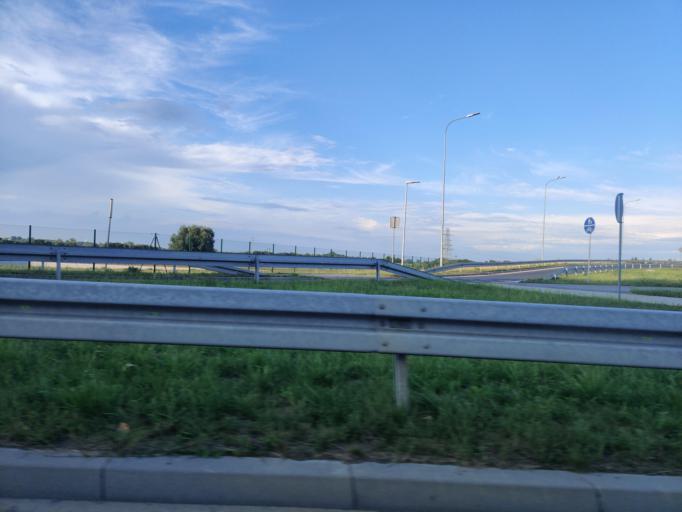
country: PL
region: Greater Poland Voivodeship
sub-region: Konin
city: Konin
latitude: 52.2044
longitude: 18.2702
